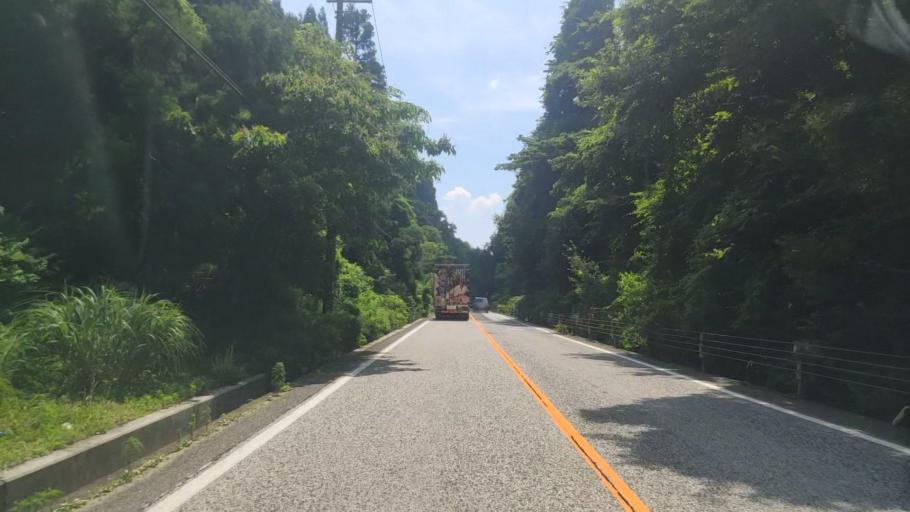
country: JP
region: Gifu
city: Tarui
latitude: 35.3762
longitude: 136.4131
